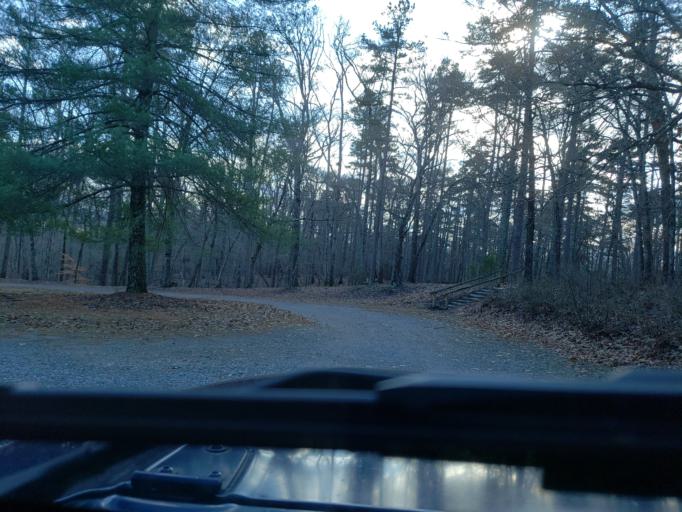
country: US
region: North Carolina
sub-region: Cleveland County
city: Kings Mountain
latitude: 35.1496
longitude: -81.3465
